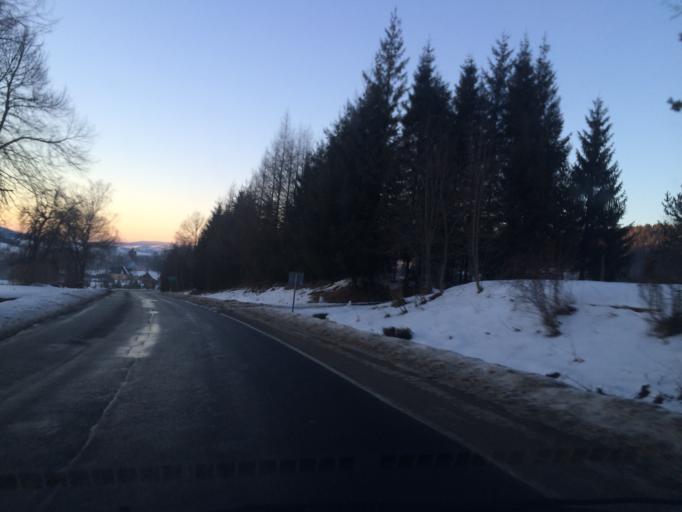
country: PL
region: Subcarpathian Voivodeship
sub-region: Powiat bieszczadzki
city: Czarna
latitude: 49.3522
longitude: 22.6828
